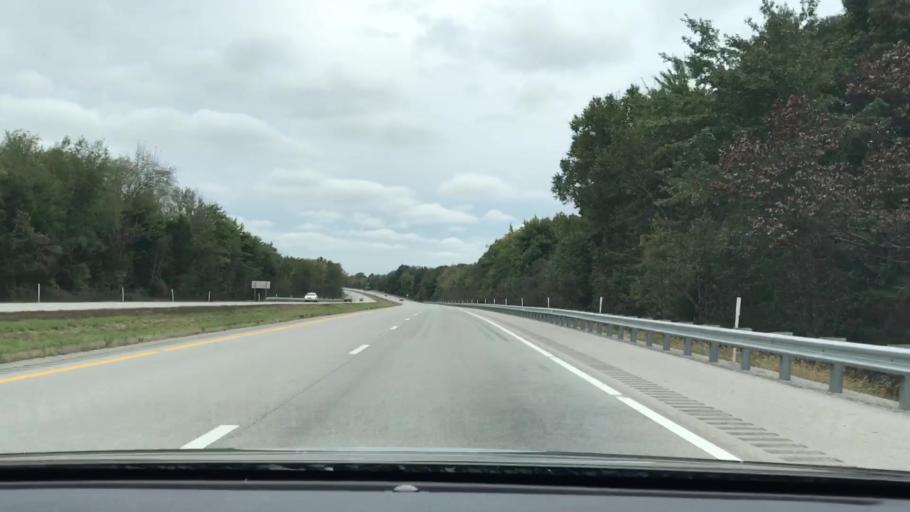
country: US
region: Kentucky
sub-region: Barren County
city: Cave City
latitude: 37.0404
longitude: -86.0639
